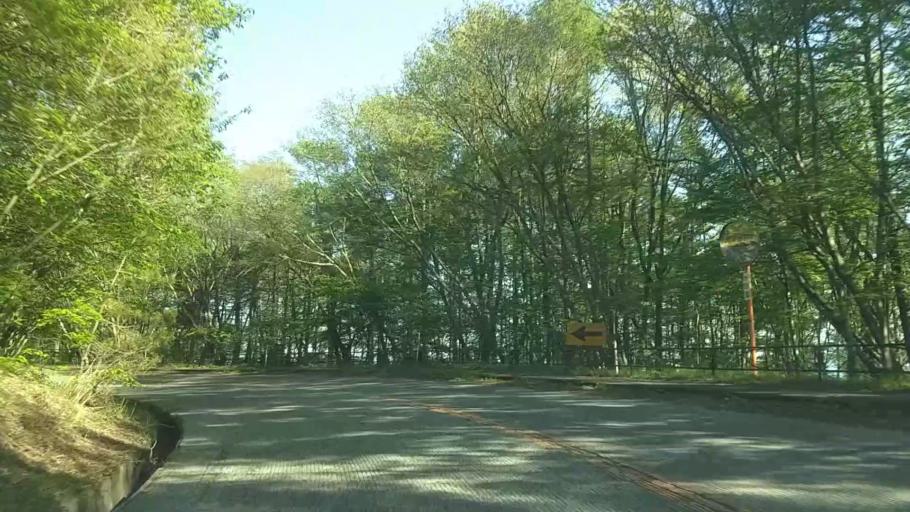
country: JP
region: Yamanashi
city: Nirasaki
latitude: 35.8986
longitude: 138.3656
